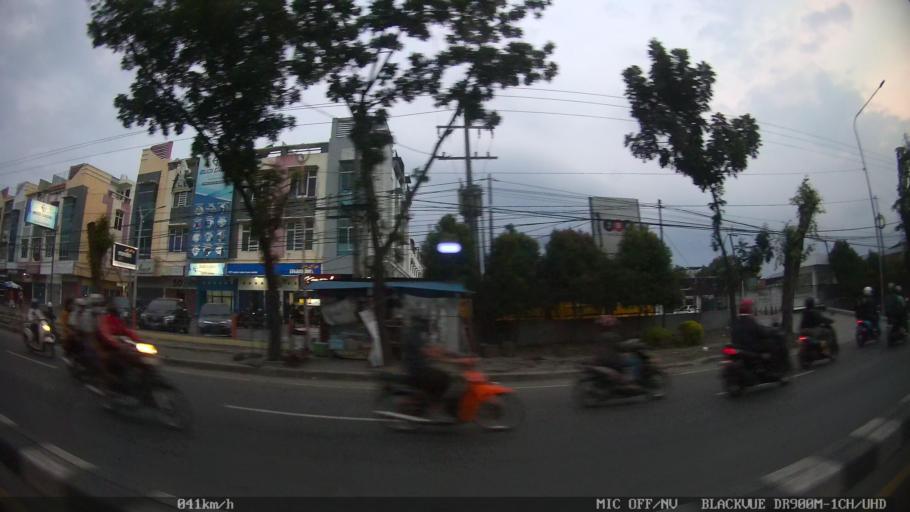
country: ID
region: North Sumatra
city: Sunggal
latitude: 3.5962
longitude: 98.6135
